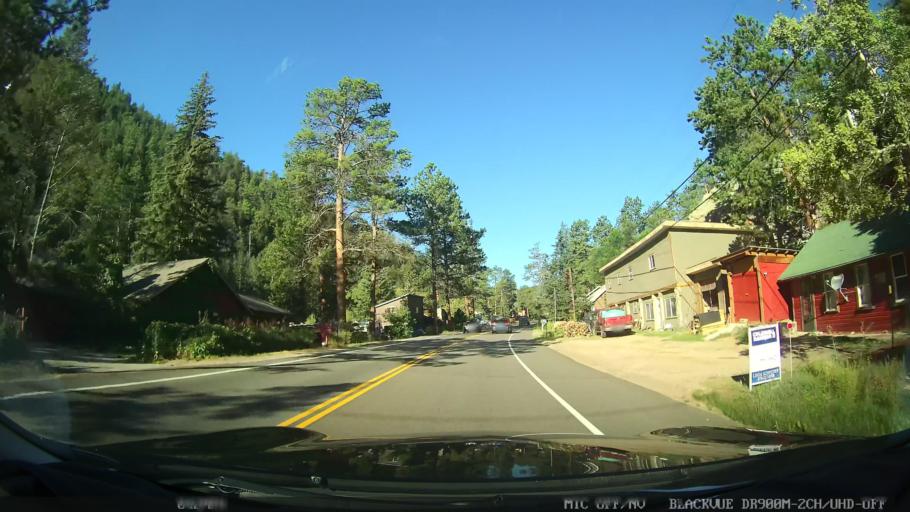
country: US
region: Colorado
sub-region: Larimer County
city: Estes Park
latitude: 40.3935
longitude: -105.4403
